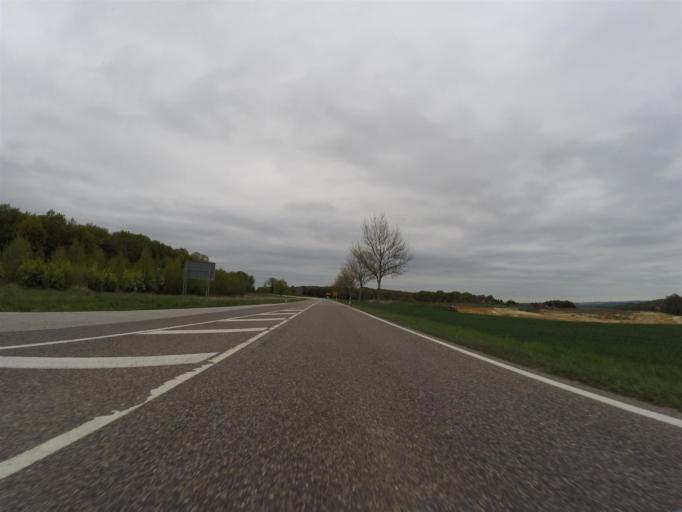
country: DE
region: Saxony-Anhalt
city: Bad Kosen
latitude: 51.1068
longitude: 11.7701
